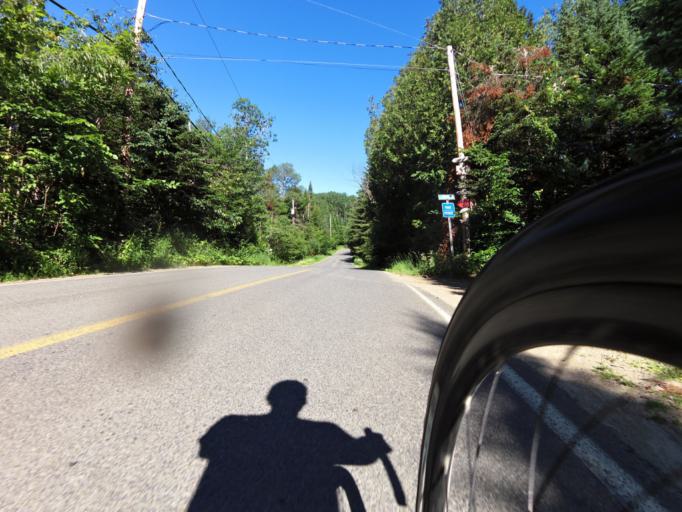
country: CA
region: Quebec
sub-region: Laurentides
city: Brownsburg-Chatham
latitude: 45.8827
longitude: -74.5724
